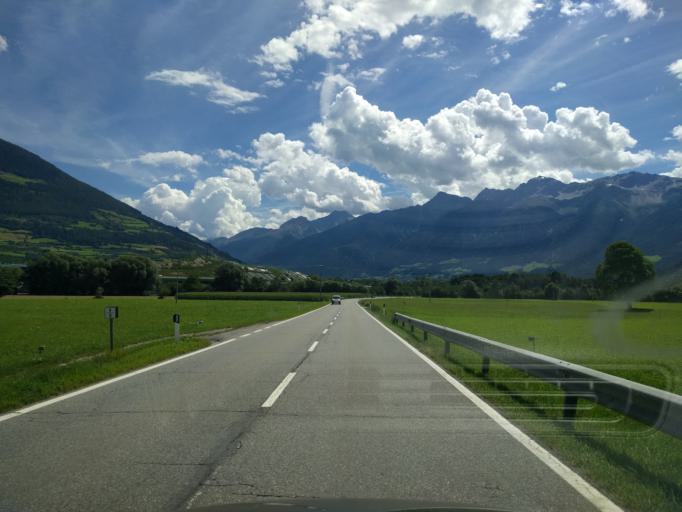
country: IT
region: Trentino-Alto Adige
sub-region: Bolzano
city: Glorenza
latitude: 46.6603
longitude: 10.5614
